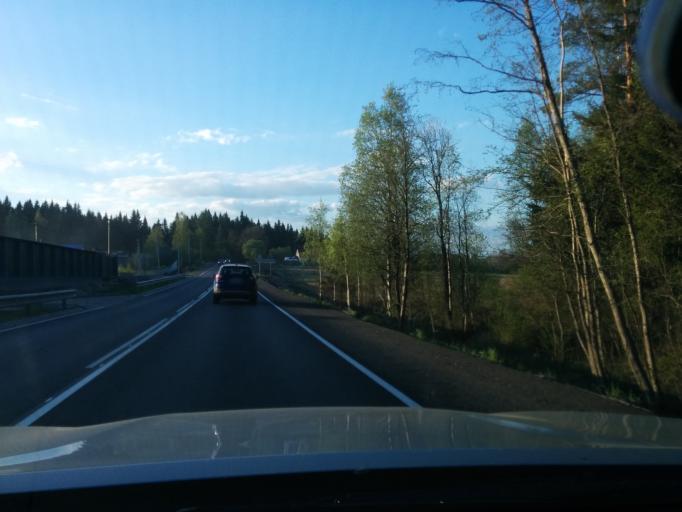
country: RU
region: Leningrad
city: Verkhniye Osel'ki
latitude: 60.2120
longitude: 30.4267
